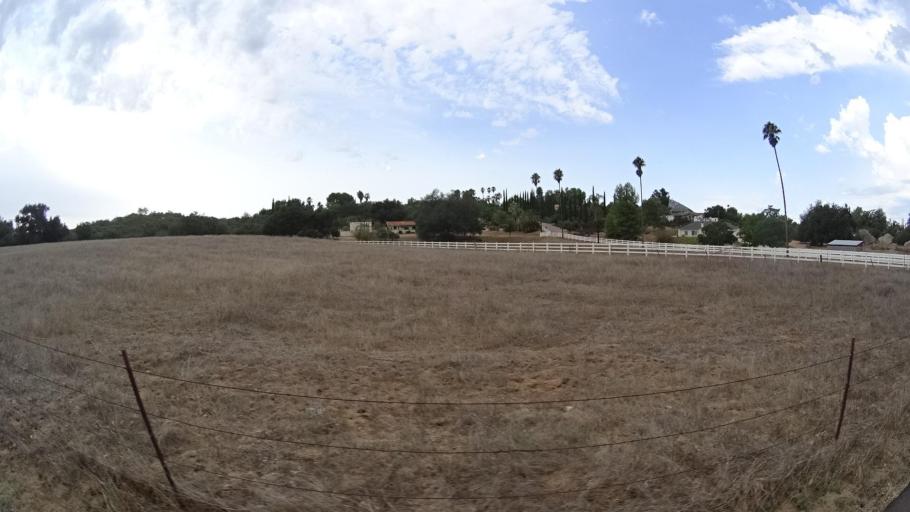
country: US
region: California
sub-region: San Diego County
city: Ramona
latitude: 33.0191
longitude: -116.9224
